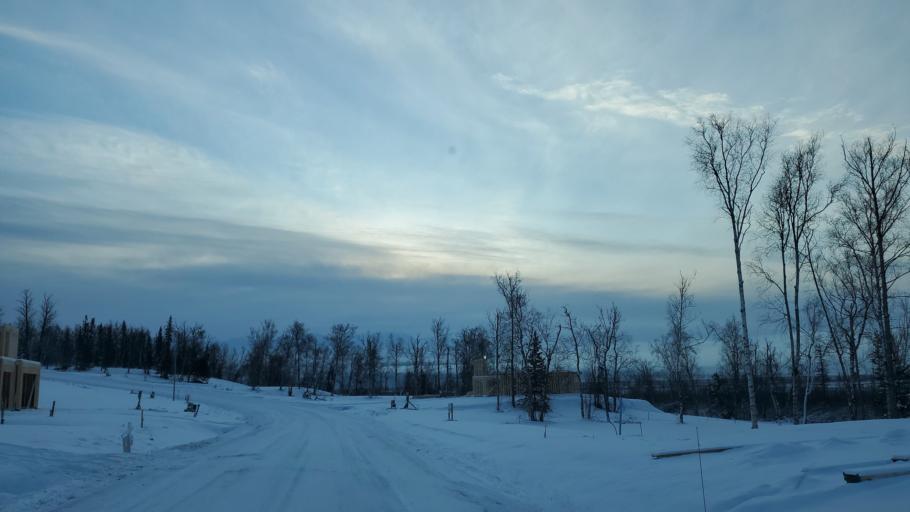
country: US
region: Alaska
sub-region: Matanuska-Susitna Borough
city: Lakes
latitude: 61.5471
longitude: -149.3270
